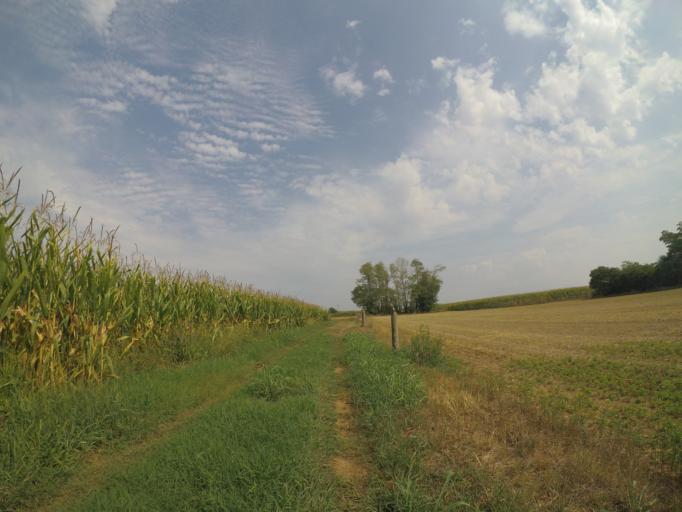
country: IT
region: Friuli Venezia Giulia
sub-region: Provincia di Udine
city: Talmassons
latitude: 45.9299
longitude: 13.1326
